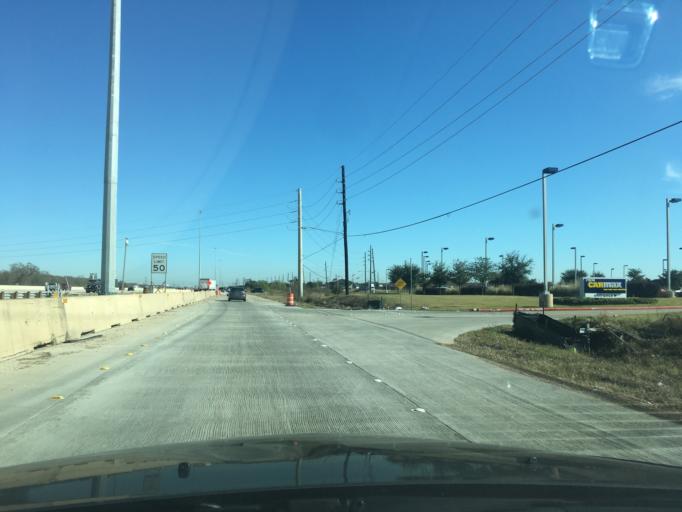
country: US
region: Texas
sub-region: Fort Bend County
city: Greatwood
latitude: 29.5568
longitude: -95.7100
